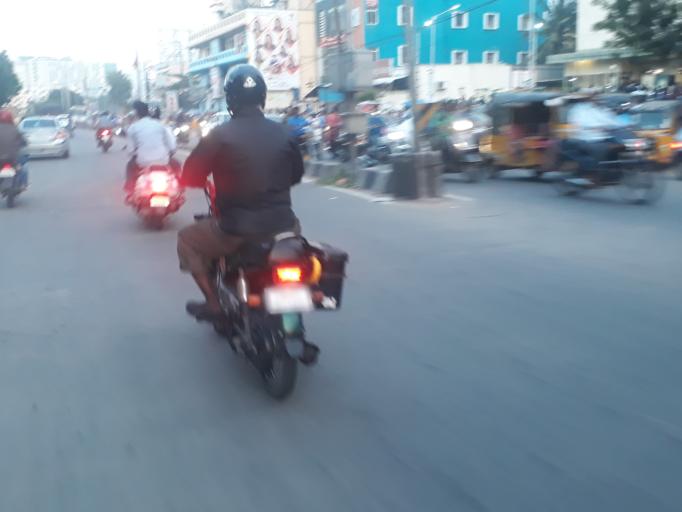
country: IN
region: Telangana
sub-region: Rangareddi
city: Uppal Kalan
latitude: 17.3999
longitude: 78.5385
